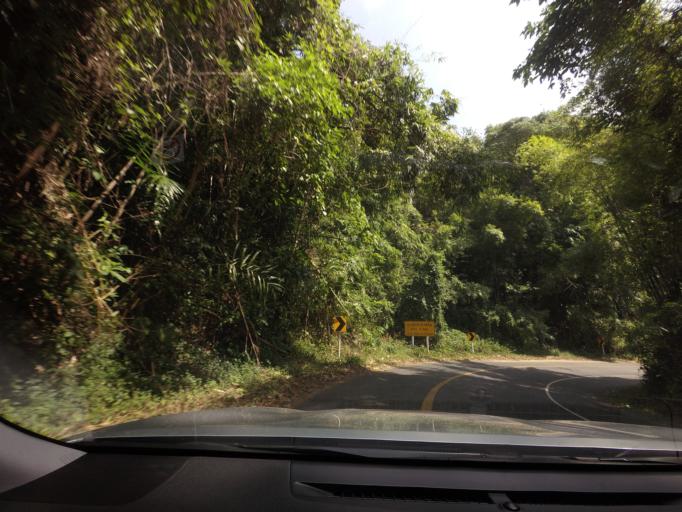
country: TH
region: Phangnga
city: Thap Put
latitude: 8.5375
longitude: 98.5617
